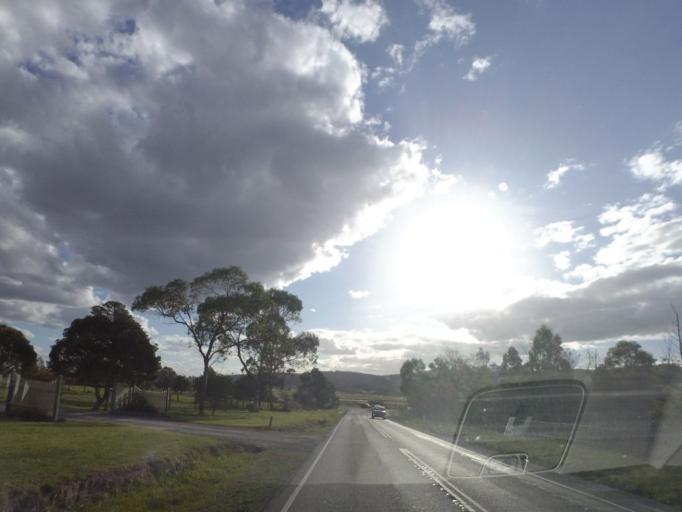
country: AU
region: Victoria
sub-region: Yarra Ranges
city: Yarra Glen
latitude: -37.6954
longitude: 145.3478
